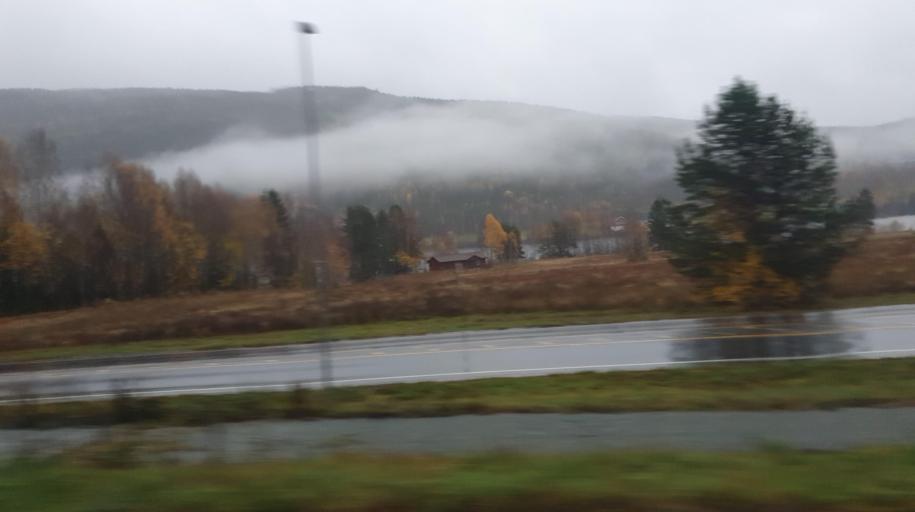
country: NO
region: Buskerud
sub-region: Krodsherad
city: Noresund
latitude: 60.1879
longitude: 9.6125
